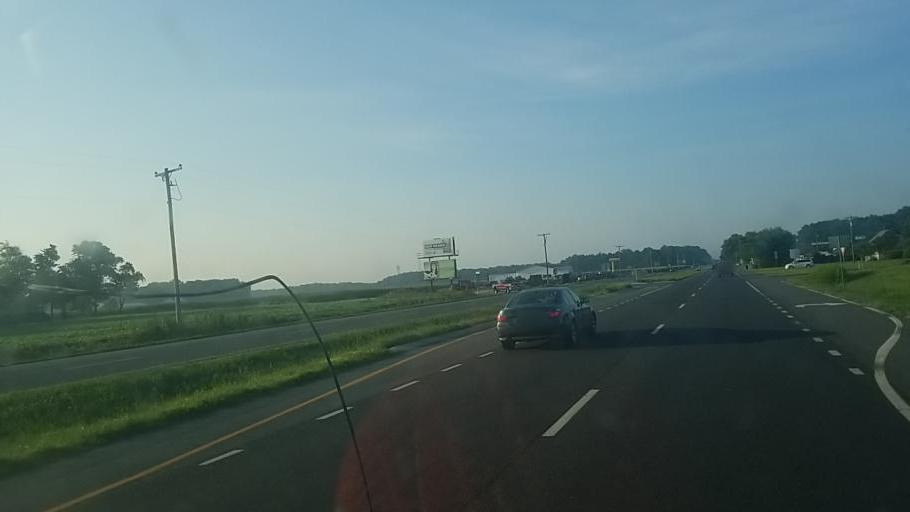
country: US
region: Delaware
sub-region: Sussex County
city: Selbyville
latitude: 38.4808
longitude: -75.2356
